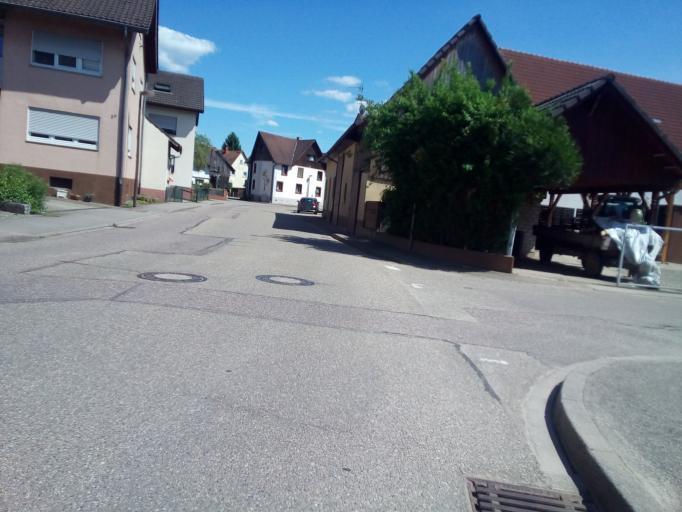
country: DE
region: Baden-Wuerttemberg
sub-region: Freiburg Region
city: Renchen
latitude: 48.6202
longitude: 7.9956
